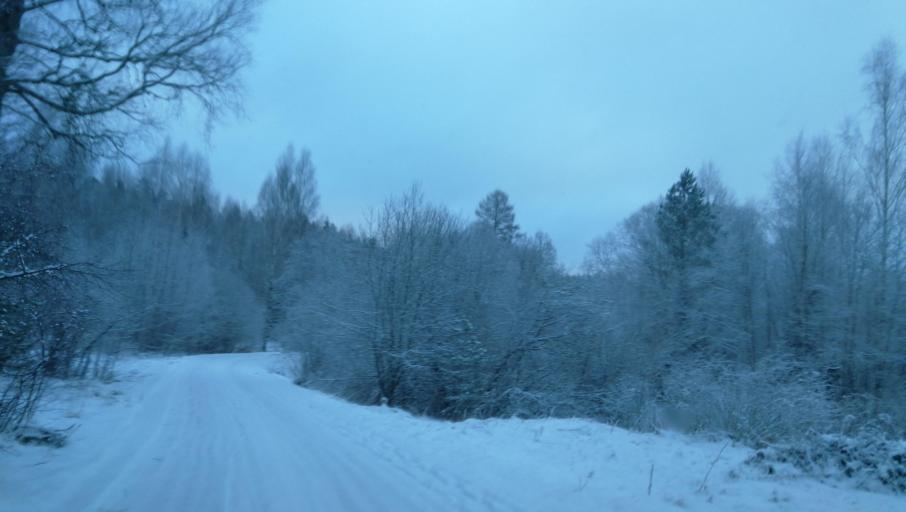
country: LV
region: Amatas Novads
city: Drabesi
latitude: 57.2098
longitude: 25.3103
